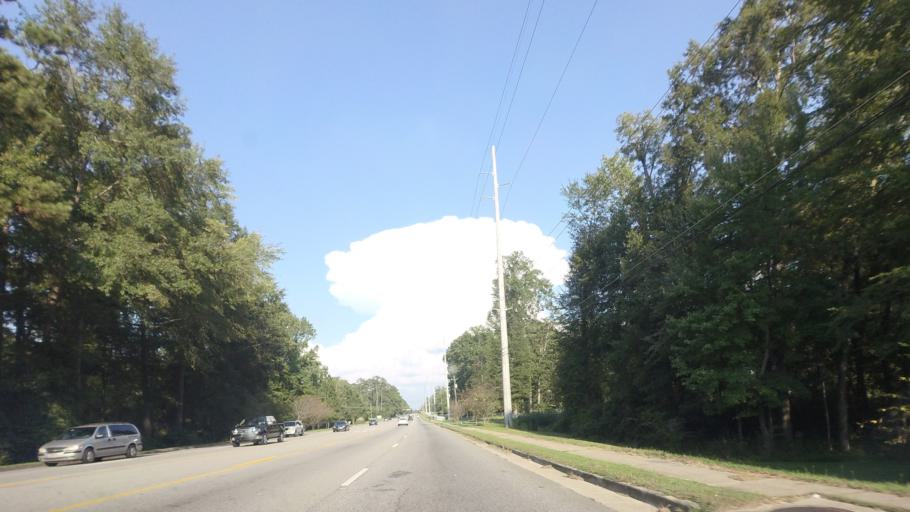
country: US
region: Georgia
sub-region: Bibb County
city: West Point
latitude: 32.8797
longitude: -83.7511
